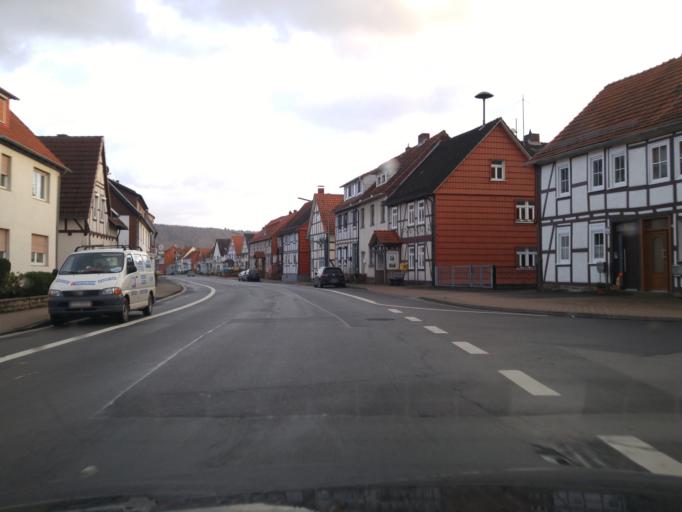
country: DE
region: Lower Saxony
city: Buhren
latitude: 51.4799
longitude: 9.6166
